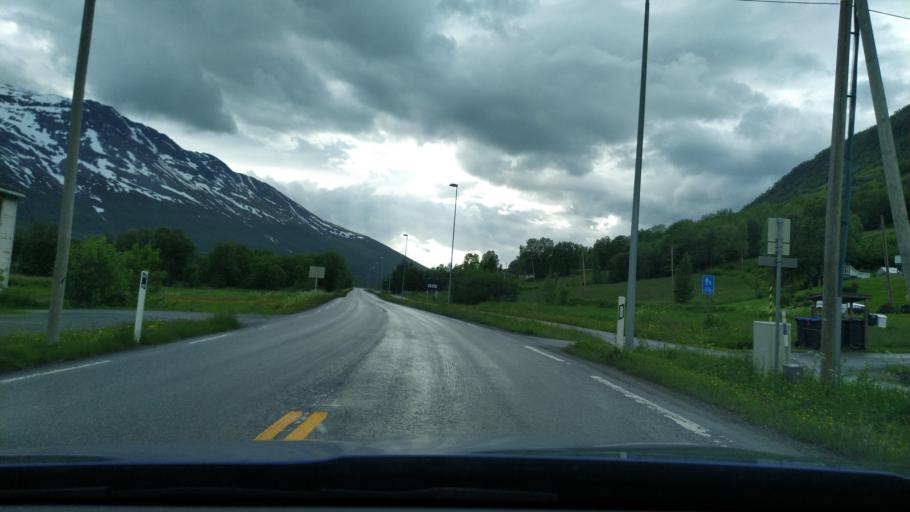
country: NO
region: Troms
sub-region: Balsfjord
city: Storsteinnes
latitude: 69.2201
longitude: 19.5512
